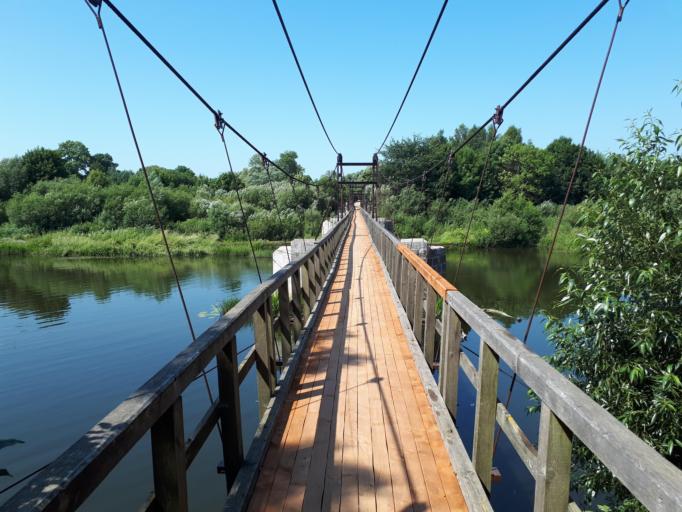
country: LT
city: Priekule
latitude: 55.4875
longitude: 21.3664
